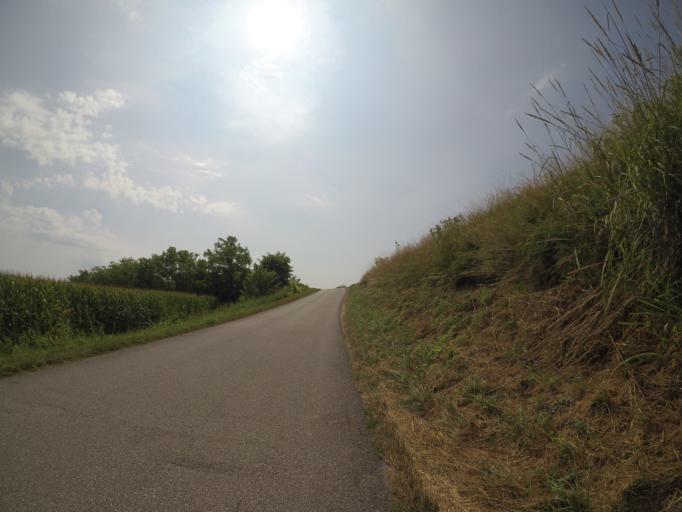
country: IT
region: Friuli Venezia Giulia
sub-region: Provincia di Udine
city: Pertegada
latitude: 45.6999
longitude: 13.0526
